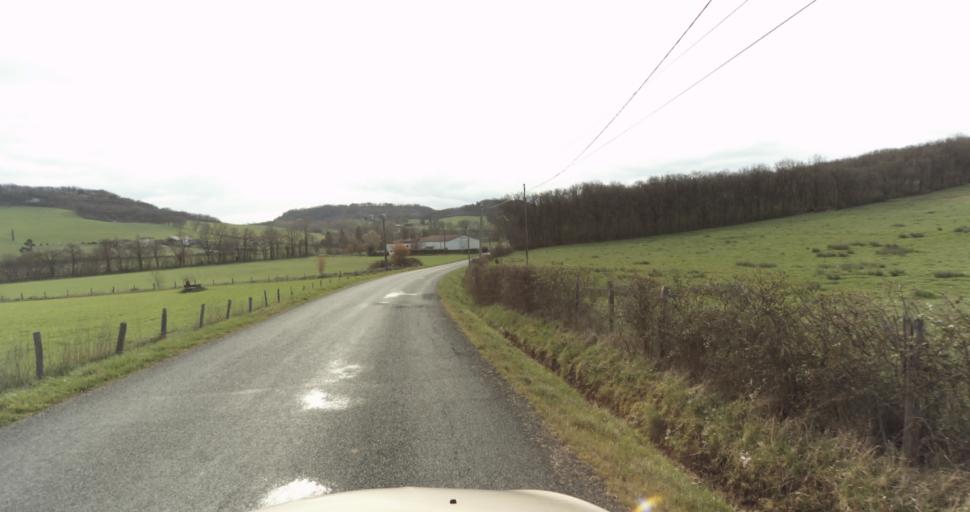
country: FR
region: Midi-Pyrenees
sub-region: Departement du Tarn
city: Puygouzon
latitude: 43.9075
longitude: 2.1809
